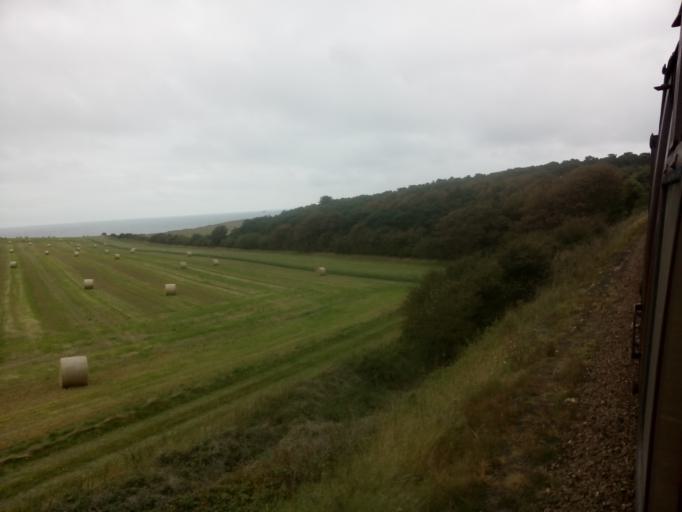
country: GB
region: England
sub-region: Norfolk
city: Sheringham
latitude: 52.9417
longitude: 1.1647
